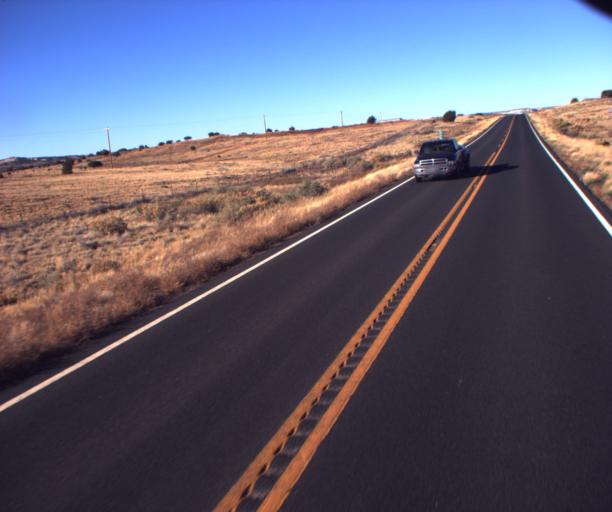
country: US
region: Arizona
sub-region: Apache County
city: Ganado
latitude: 35.7857
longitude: -109.6997
